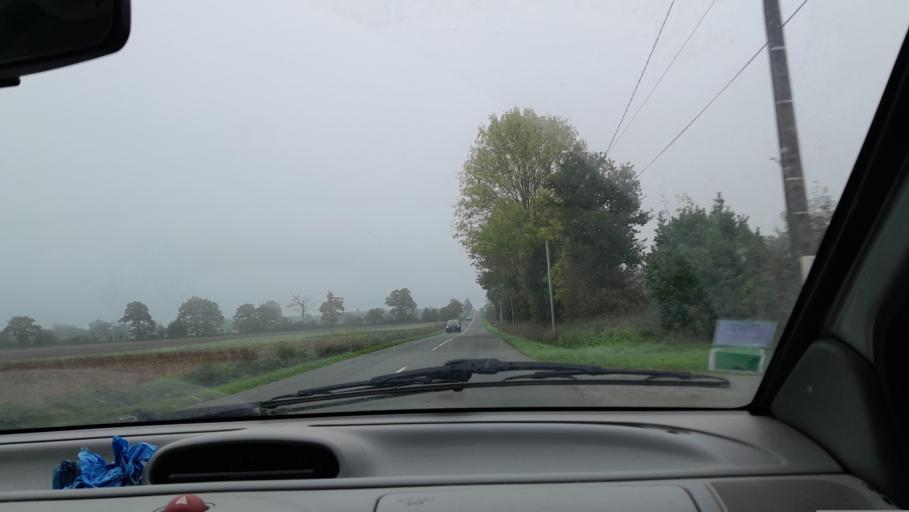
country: FR
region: Pays de la Loire
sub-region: Departement de la Mayenne
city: Ahuille
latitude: 48.0429
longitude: -0.8828
